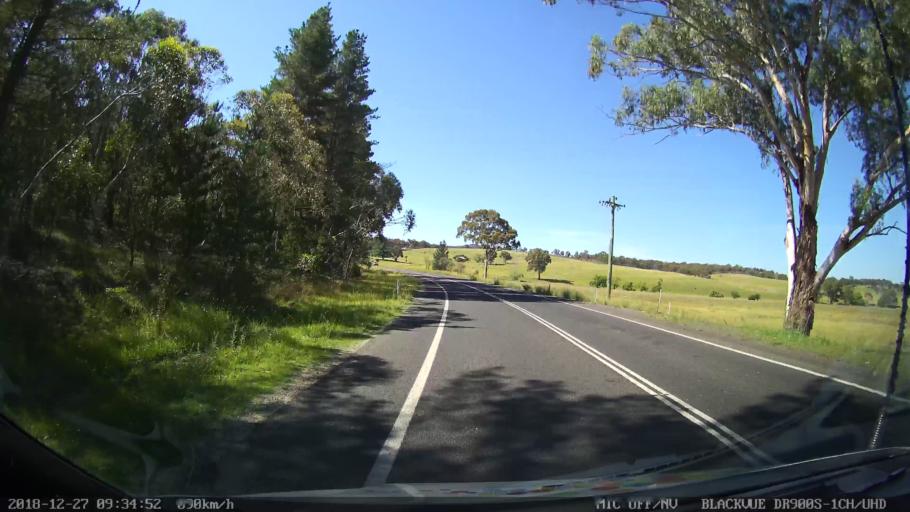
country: AU
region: New South Wales
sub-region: Lithgow
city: Portland
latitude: -33.2319
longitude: 150.0262
